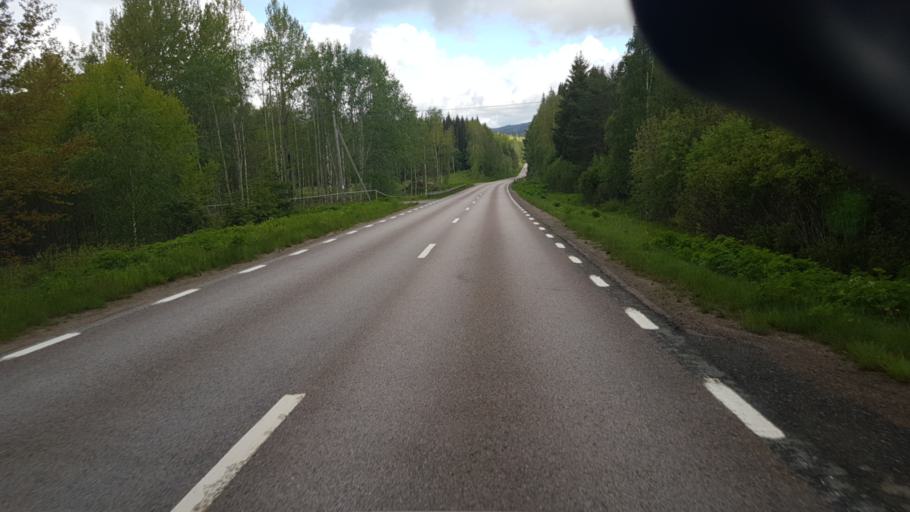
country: SE
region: Vaermland
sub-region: Eda Kommun
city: Amotfors
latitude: 59.7032
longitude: 12.3100
